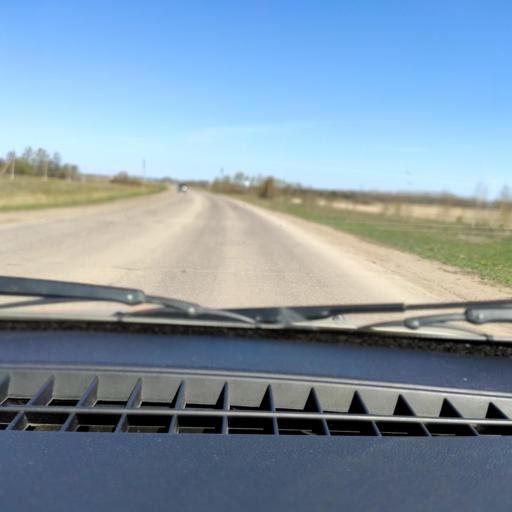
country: RU
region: Bashkortostan
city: Iglino
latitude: 54.7875
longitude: 56.4182
